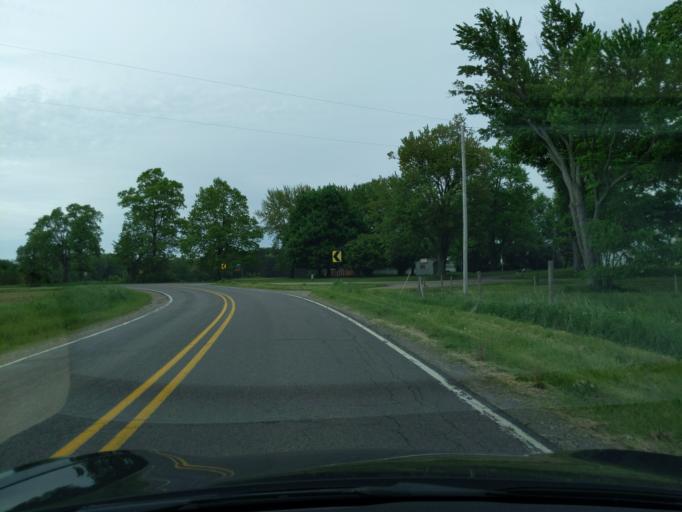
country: US
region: Michigan
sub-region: Ingham County
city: Leslie
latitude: 42.4568
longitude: -84.3519
